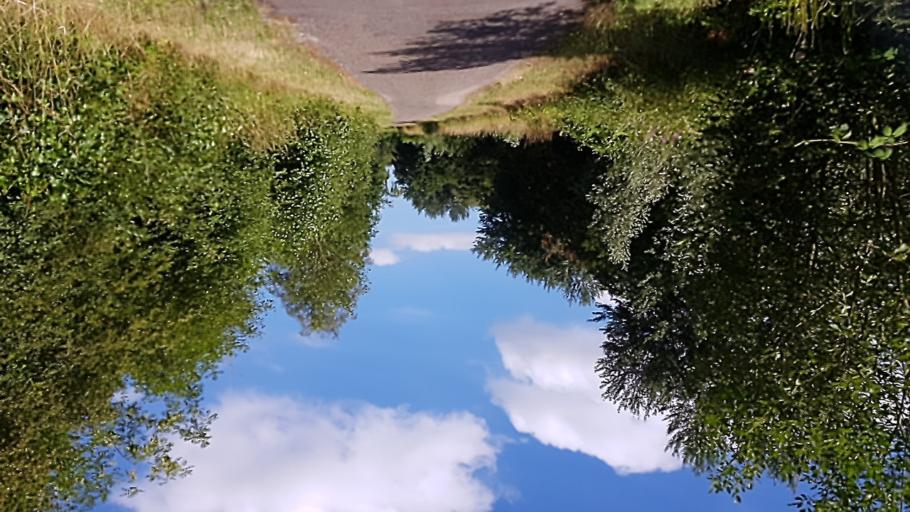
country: BE
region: Wallonia
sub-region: Province du Brabant Wallon
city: Court-Saint-Etienne
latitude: 50.6207
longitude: 4.5238
